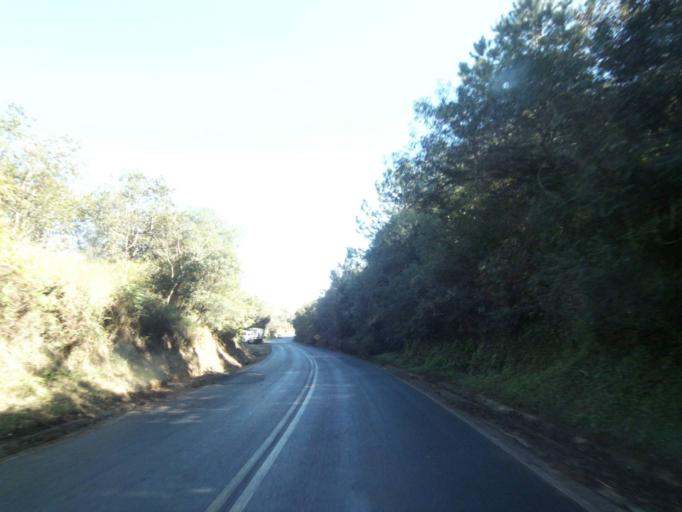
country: BR
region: Parana
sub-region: Tibagi
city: Tibagi
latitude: -24.5277
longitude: -50.3926
